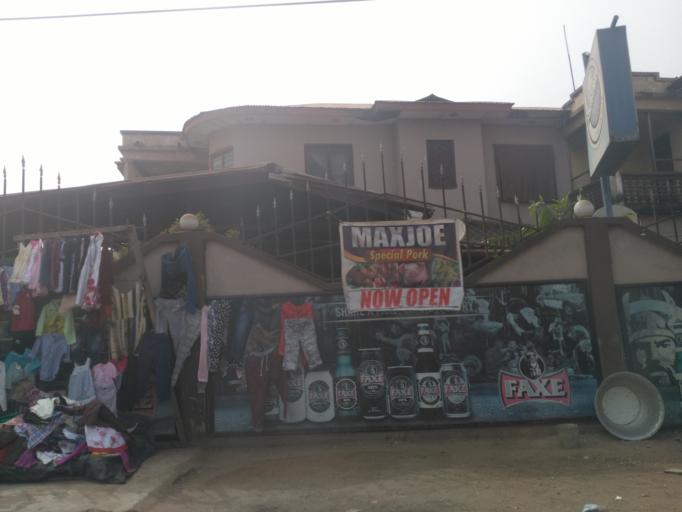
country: GH
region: Ashanti
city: Kumasi
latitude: 6.7041
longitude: -1.6233
